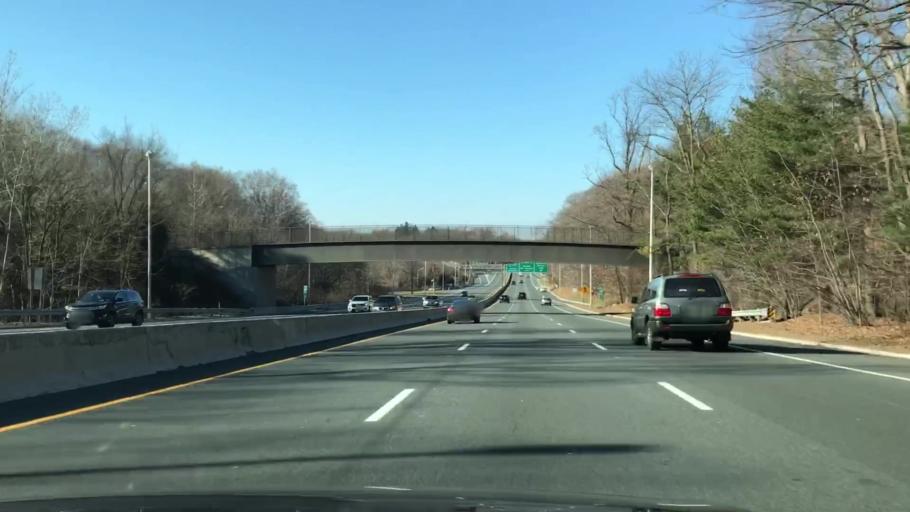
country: US
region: New Jersey
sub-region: Bergen County
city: Franklin Lakes
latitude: 41.0158
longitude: -74.2127
